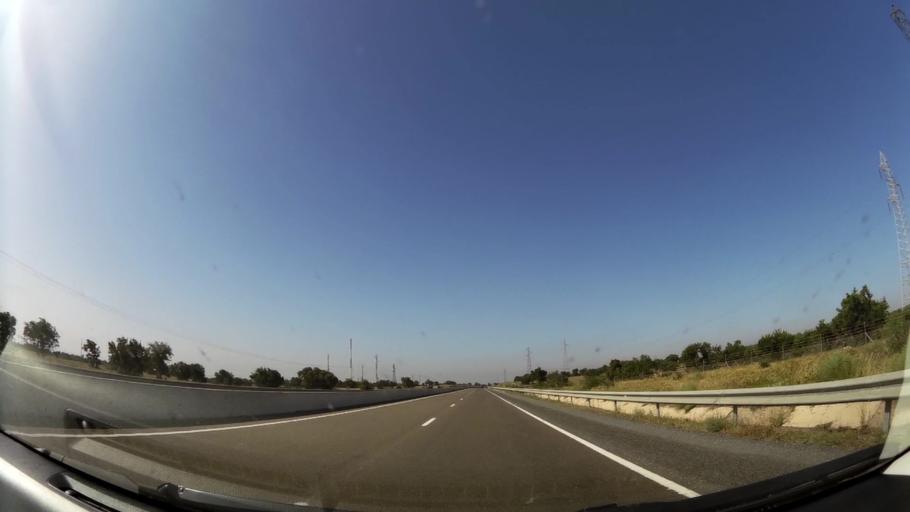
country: MA
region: Souss-Massa-Draa
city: Oulad Teima
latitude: 30.4369
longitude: -9.3705
